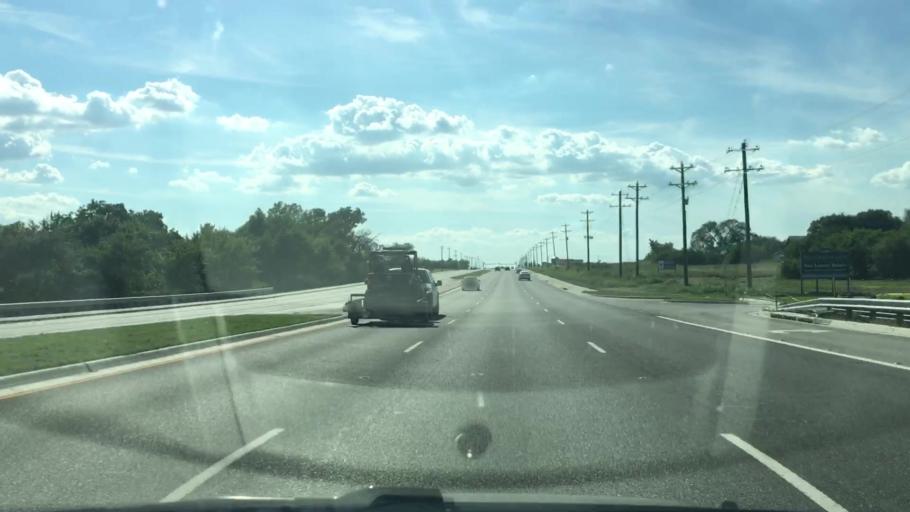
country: US
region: Texas
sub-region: Collin County
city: Prosper
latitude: 33.2187
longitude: -96.7560
